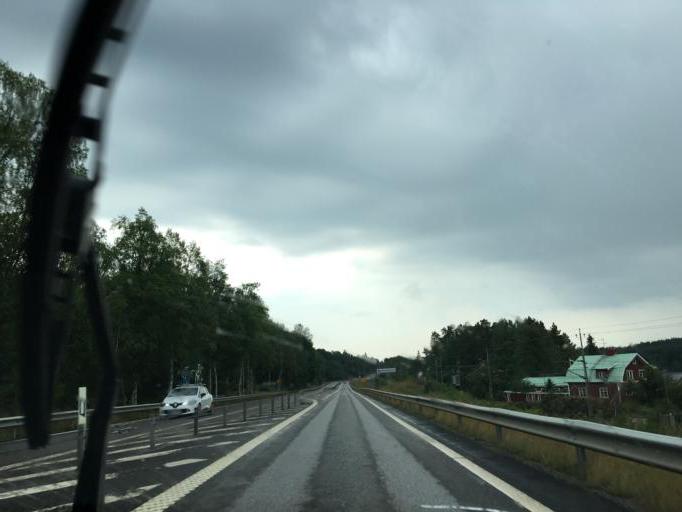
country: SE
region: OEstergoetland
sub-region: Norrkopings Kommun
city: Jursla
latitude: 58.7816
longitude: 16.1593
